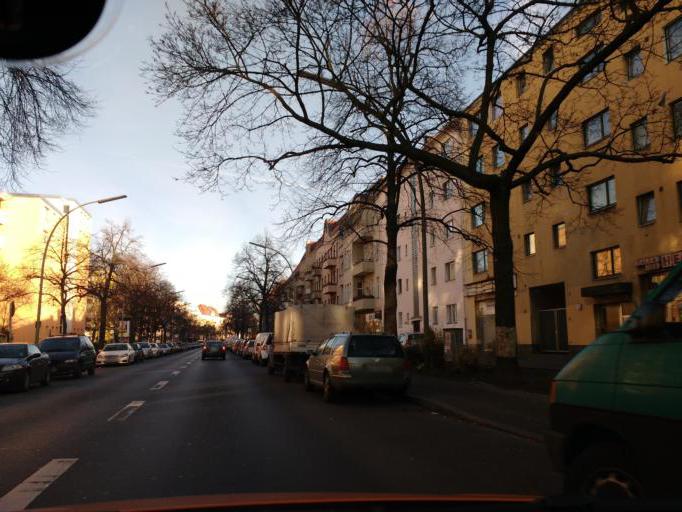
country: DE
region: Berlin
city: Gesundbrunnen
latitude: 52.5608
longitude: 13.3879
